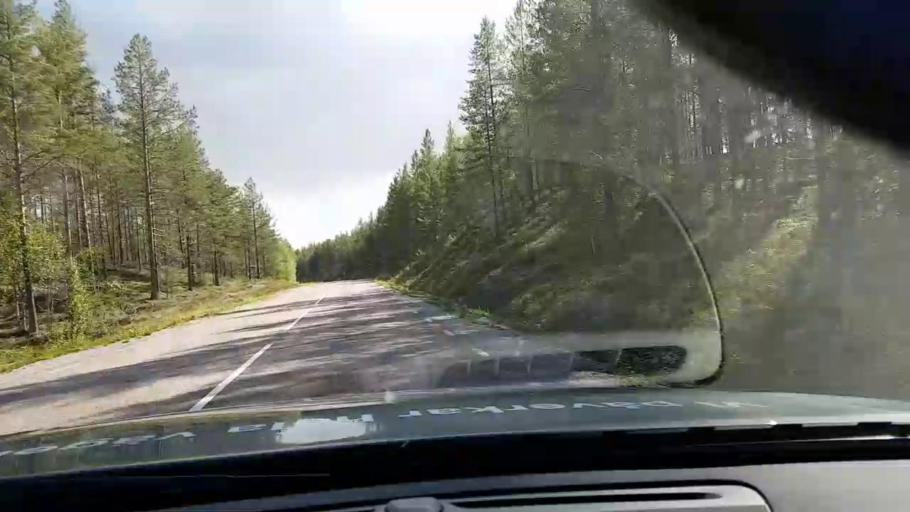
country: SE
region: Vaesterbotten
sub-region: Asele Kommun
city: Asele
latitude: 63.8820
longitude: 17.3541
